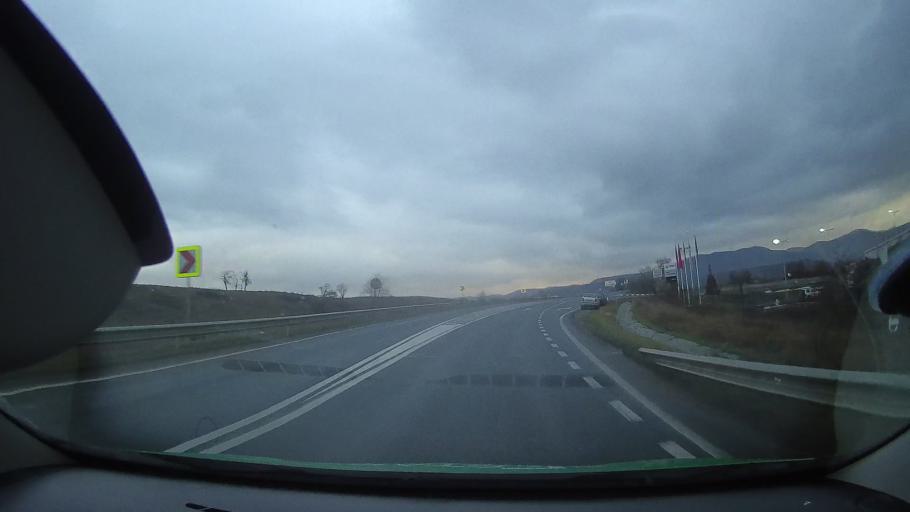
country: RO
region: Hunedoara
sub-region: Comuna Ribita
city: Ribita
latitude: 46.1648
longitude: 22.7533
